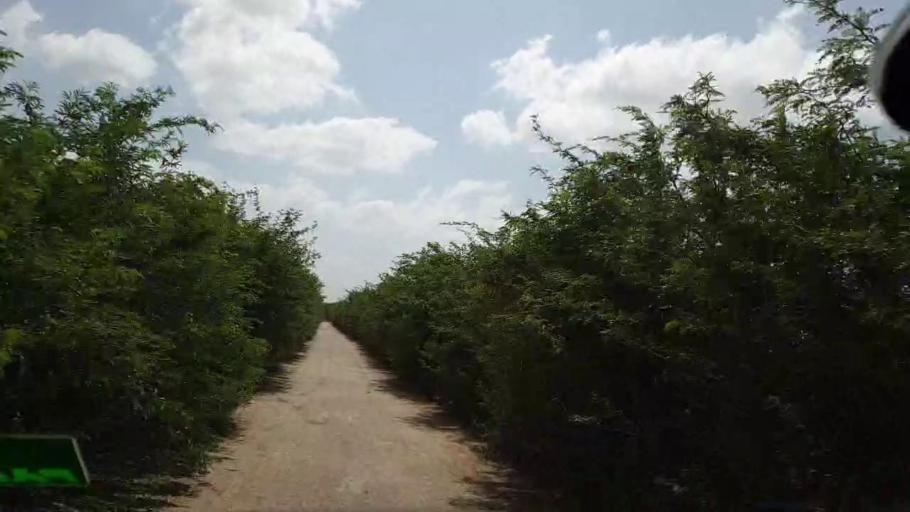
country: PK
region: Sindh
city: Kadhan
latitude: 24.5447
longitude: 69.2070
